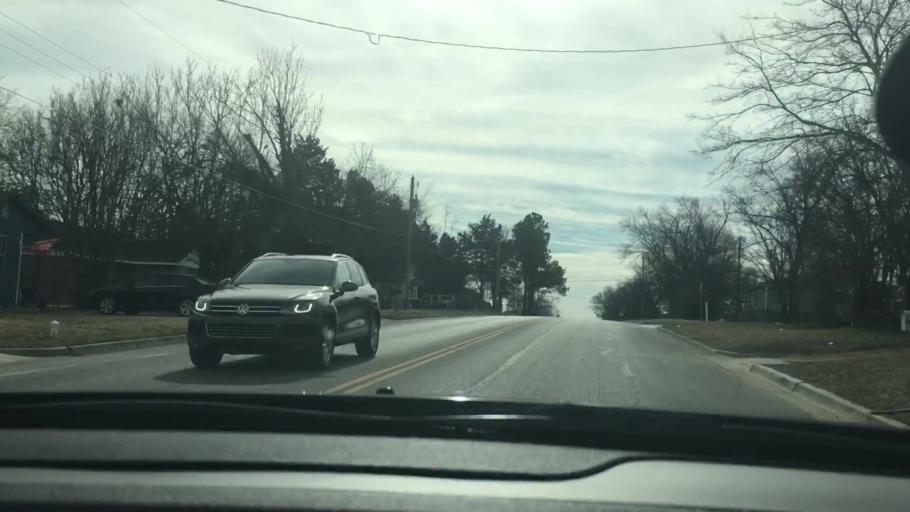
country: US
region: Oklahoma
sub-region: Carter County
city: Ardmore
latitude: 34.1757
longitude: -97.1082
